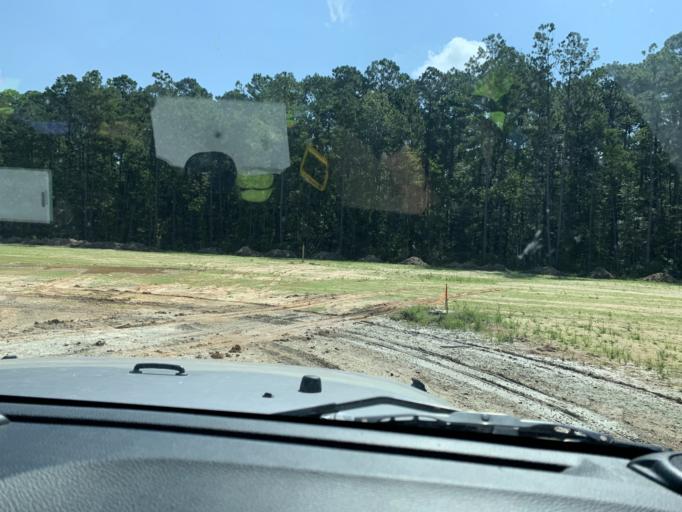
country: US
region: Georgia
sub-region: Chatham County
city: Bloomingdale
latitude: 32.1336
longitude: -81.2903
